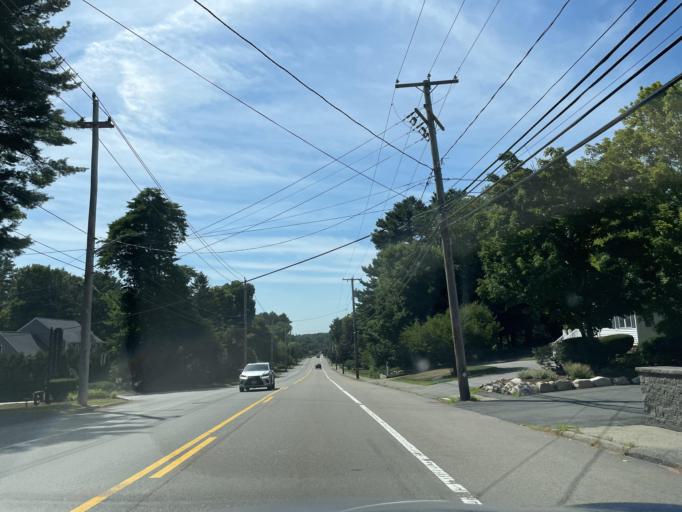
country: US
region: Massachusetts
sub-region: Norfolk County
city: Foxborough
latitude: 42.0755
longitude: -71.2683
